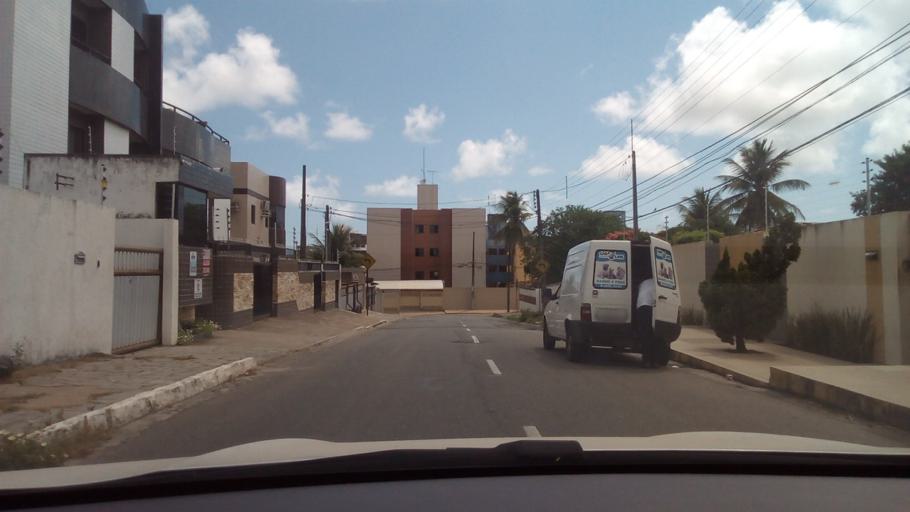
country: BR
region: Paraiba
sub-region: Joao Pessoa
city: Joao Pessoa
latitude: -7.1524
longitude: -34.8460
